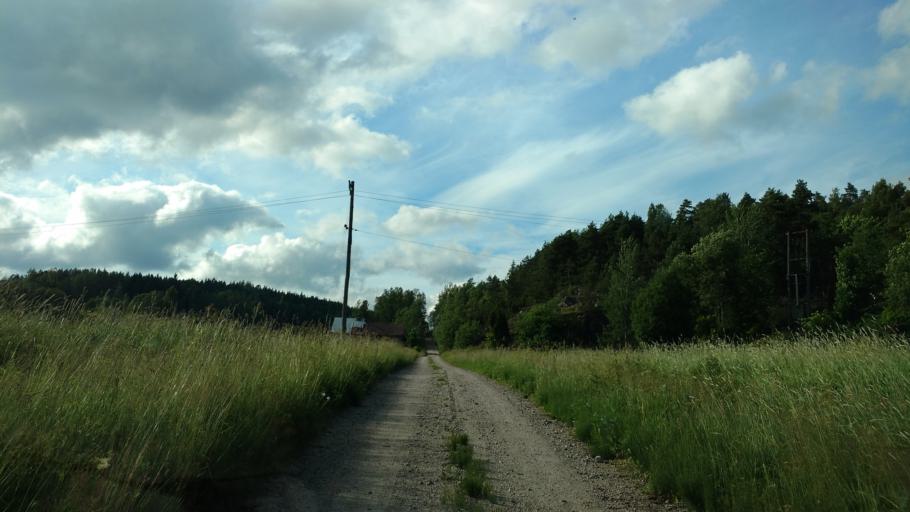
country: FI
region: Varsinais-Suomi
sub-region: Salo
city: Salo
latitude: 60.4248
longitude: 23.1761
